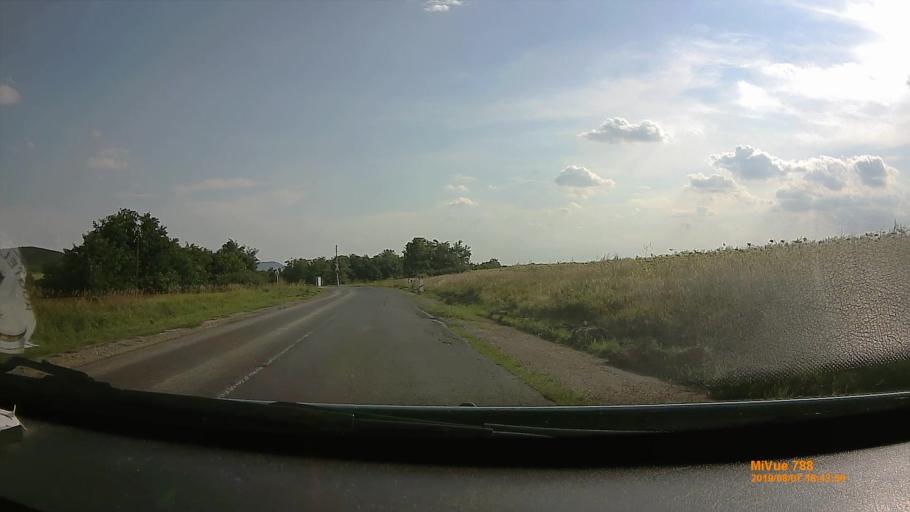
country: HU
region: Borsod-Abauj-Zemplen
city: Abaujszanto
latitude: 48.3501
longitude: 21.2120
